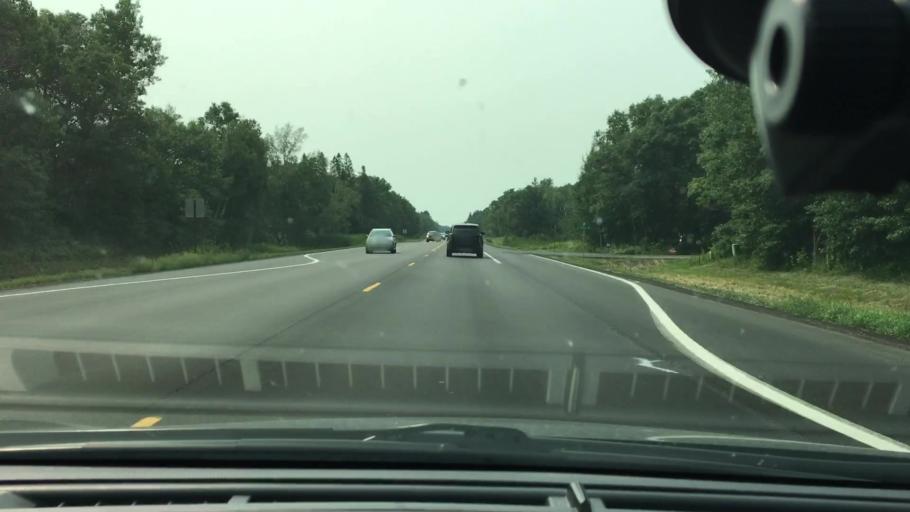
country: US
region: Minnesota
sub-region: Crow Wing County
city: Brainerd
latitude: 46.4562
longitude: -94.1723
